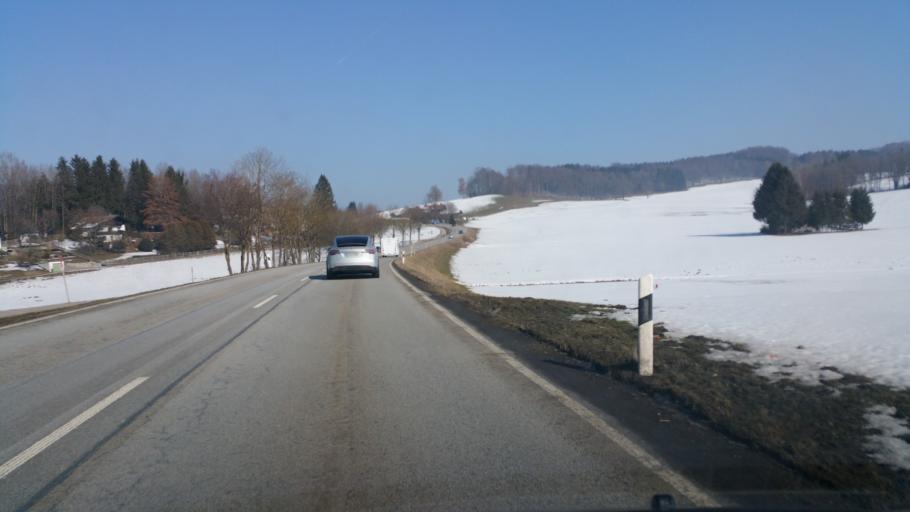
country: DE
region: Bavaria
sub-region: Upper Bavaria
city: Miesbach
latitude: 47.7970
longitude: 11.8443
